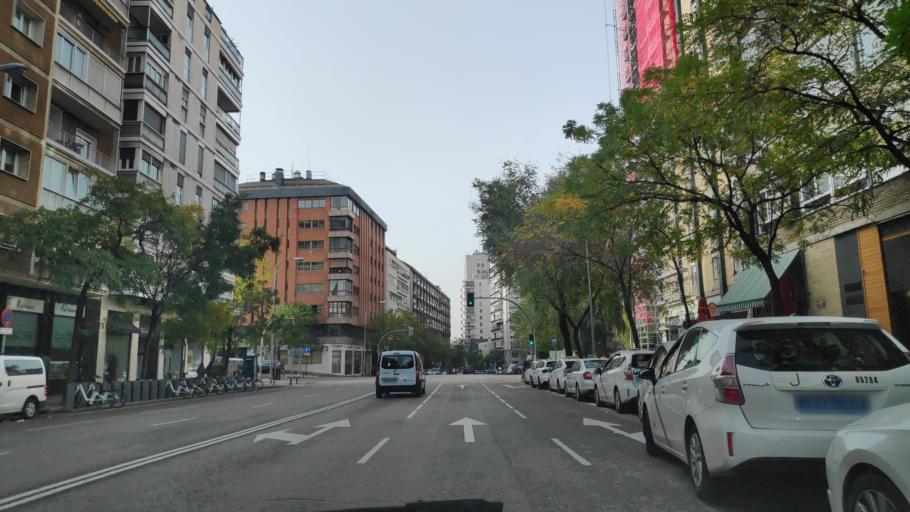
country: ES
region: Madrid
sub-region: Provincia de Madrid
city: Chamartin
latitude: 40.4502
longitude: -3.6877
